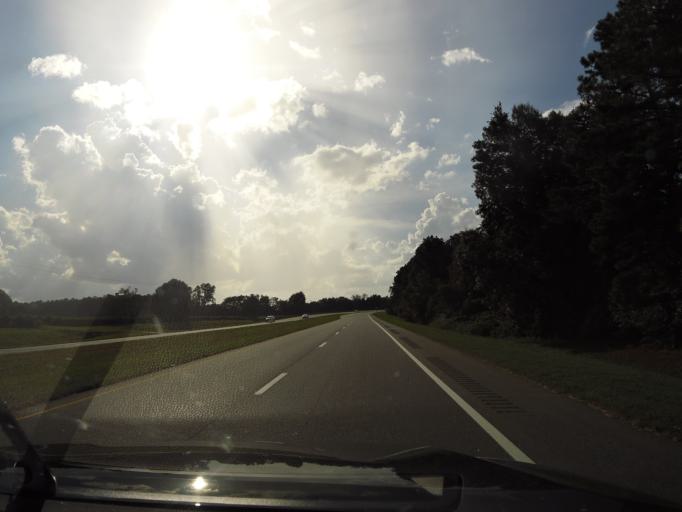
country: US
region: Georgia
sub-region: Brooks County
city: Quitman
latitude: 30.7850
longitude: -83.6194
